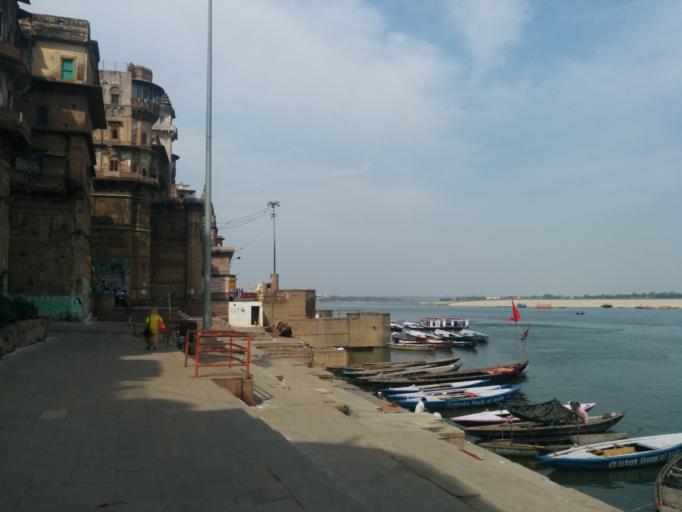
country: IN
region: Uttar Pradesh
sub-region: Varanasi
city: Varanasi
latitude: 25.3047
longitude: 83.0090
